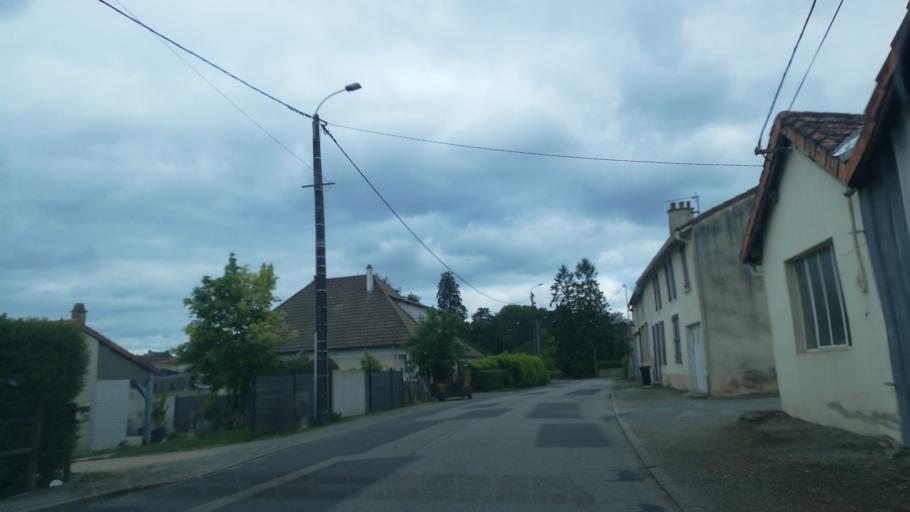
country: FR
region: Poitou-Charentes
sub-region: Departement des Deux-Sevres
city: La Chapelle-Saint-Laurent
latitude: 46.7467
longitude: -0.4820
